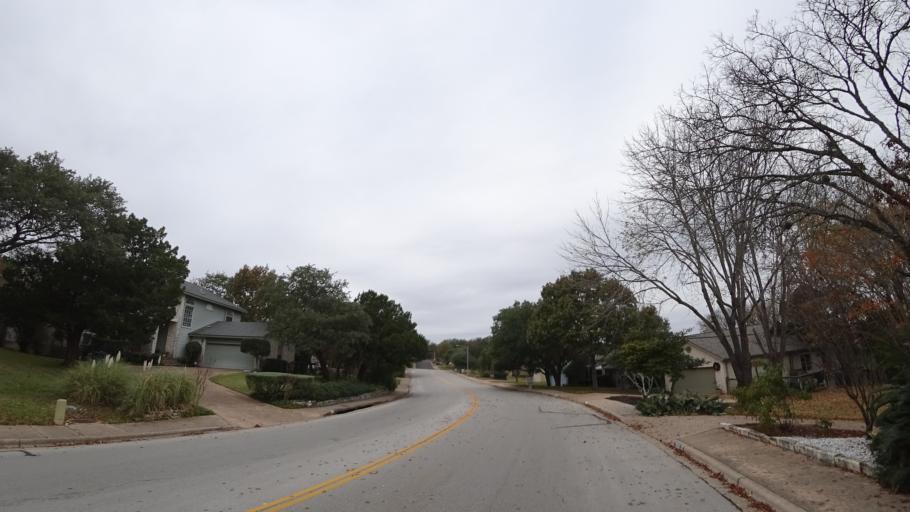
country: US
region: Texas
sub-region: Williamson County
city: Jollyville
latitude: 30.3776
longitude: -97.7959
